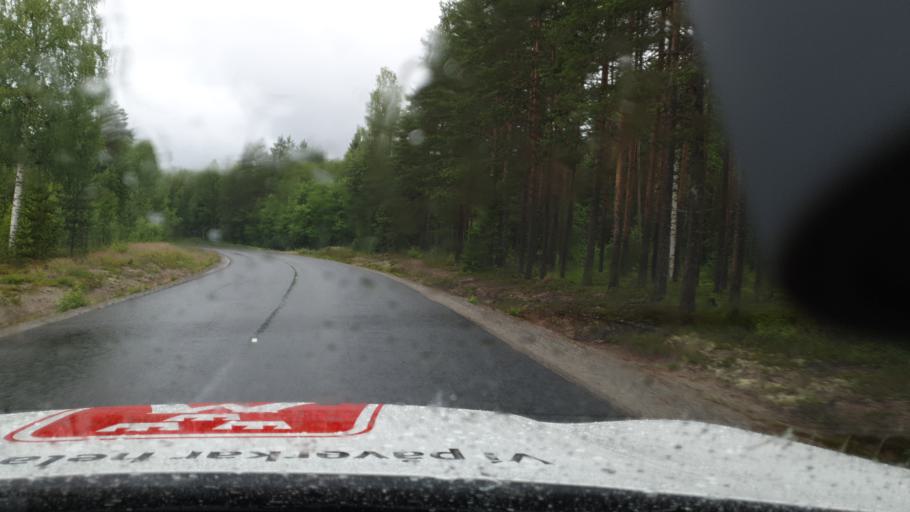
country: SE
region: Vaesterbotten
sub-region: Vindelns Kommun
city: Vindeln
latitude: 64.2745
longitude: 19.6336
